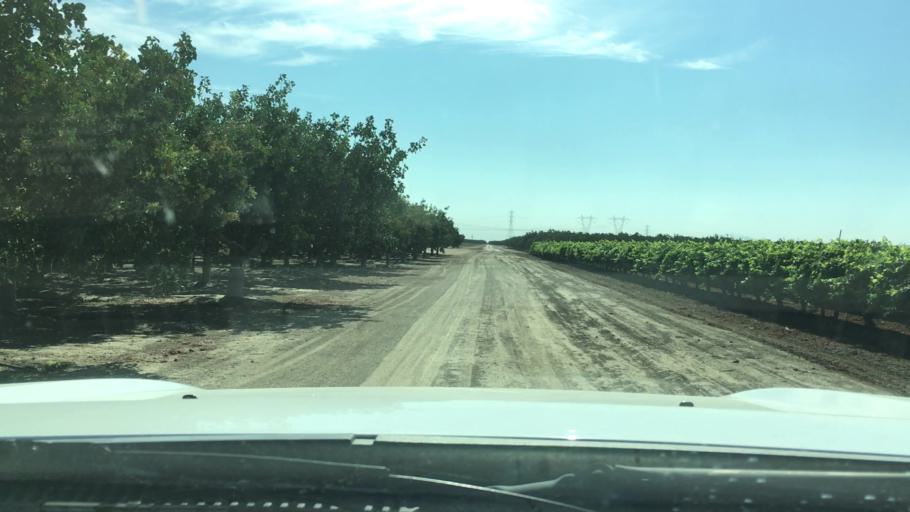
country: US
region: California
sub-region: Kern County
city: Buttonwillow
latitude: 35.3658
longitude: -119.3874
